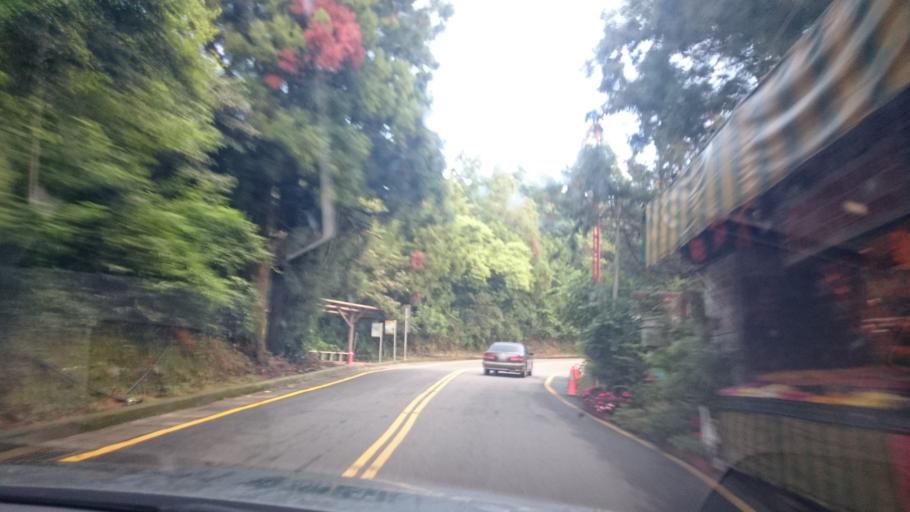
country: TW
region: Taiwan
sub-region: Nantou
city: Puli
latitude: 24.0441
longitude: 121.1558
